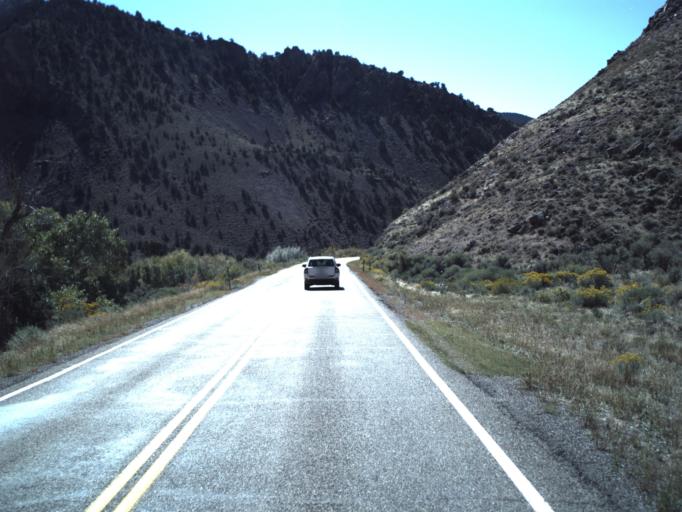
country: US
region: Utah
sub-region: Piute County
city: Junction
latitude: 38.1956
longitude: -112.1265
